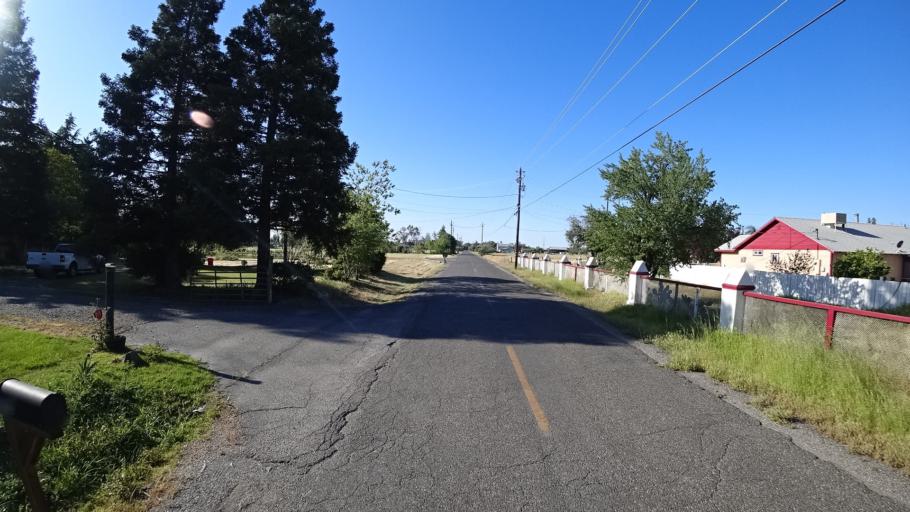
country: US
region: California
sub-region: Glenn County
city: Orland
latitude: 39.7289
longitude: -122.1876
